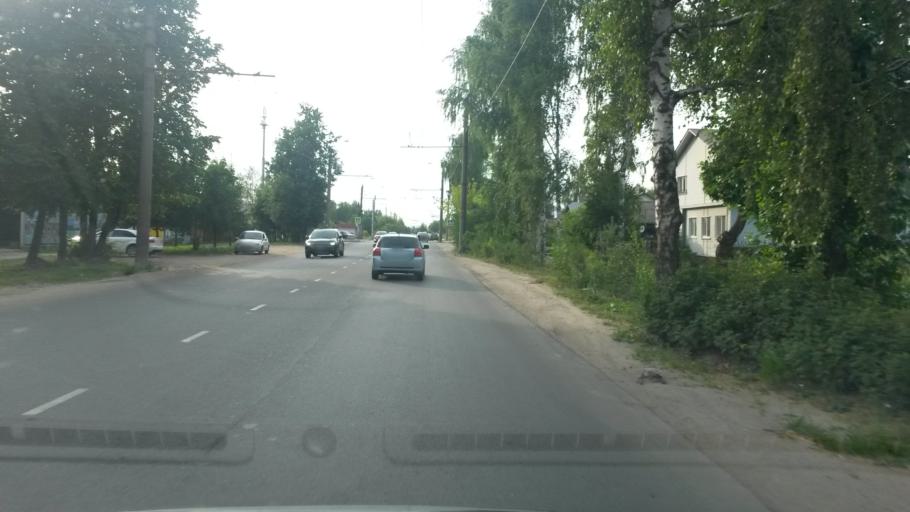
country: RU
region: Ivanovo
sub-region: Gorod Ivanovo
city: Ivanovo
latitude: 57.0151
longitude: 40.9306
